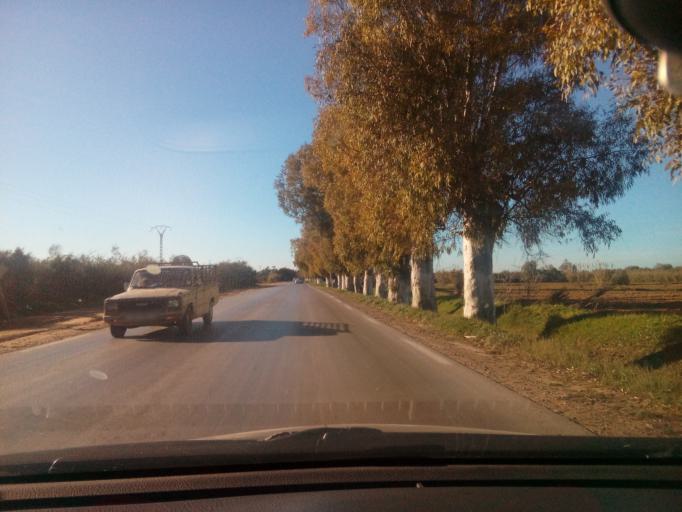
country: DZ
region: Mostaganem
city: Mostaganem
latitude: 35.9005
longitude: 0.2230
